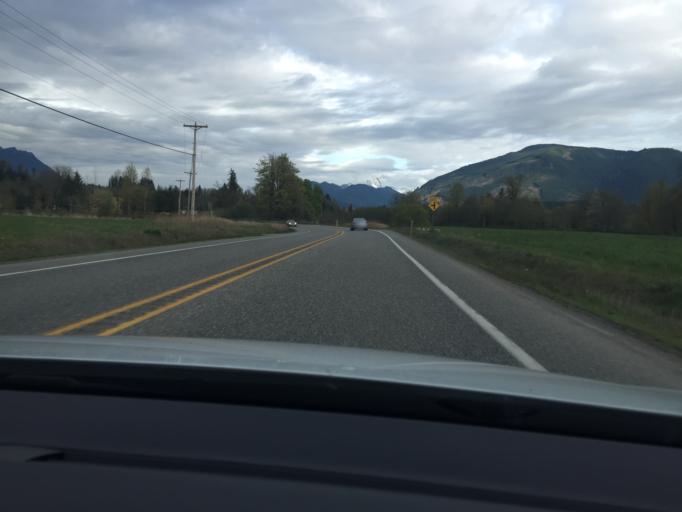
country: US
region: Washington
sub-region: Snohomish County
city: Arlington Heights
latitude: 48.2737
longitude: -121.9908
